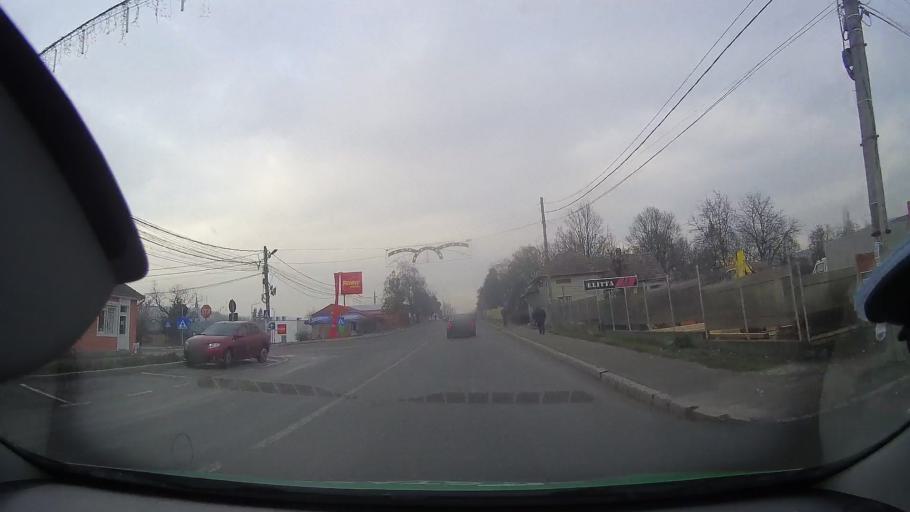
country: RO
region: Mures
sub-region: Comuna Ludus
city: Ludus
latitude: 46.4781
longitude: 24.0957
